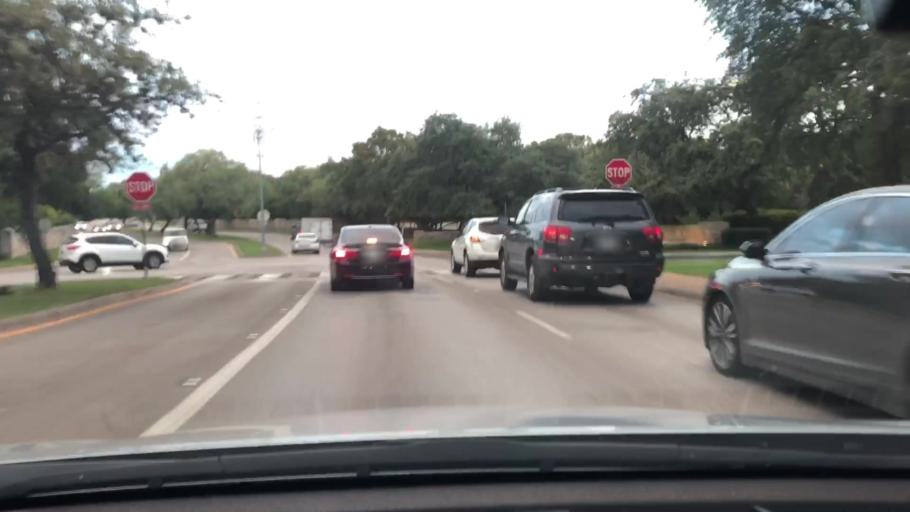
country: US
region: Texas
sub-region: Bexar County
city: Shavano Park
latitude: 29.5948
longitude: -98.5335
